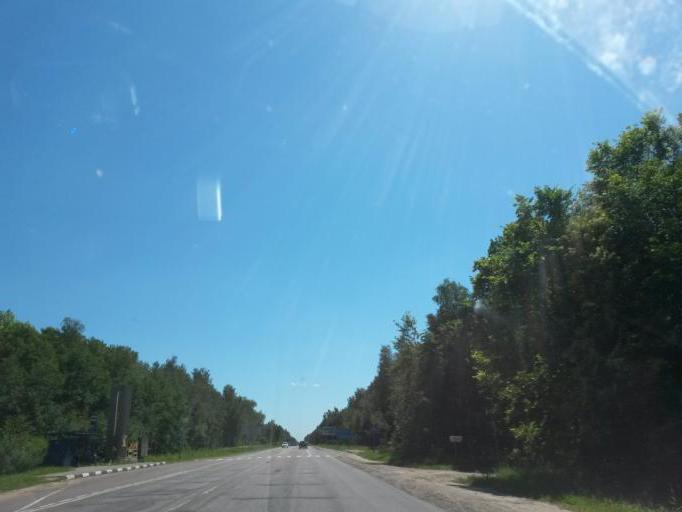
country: RU
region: Moskovskaya
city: Proletarskiy
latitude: 55.0621
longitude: 37.4354
